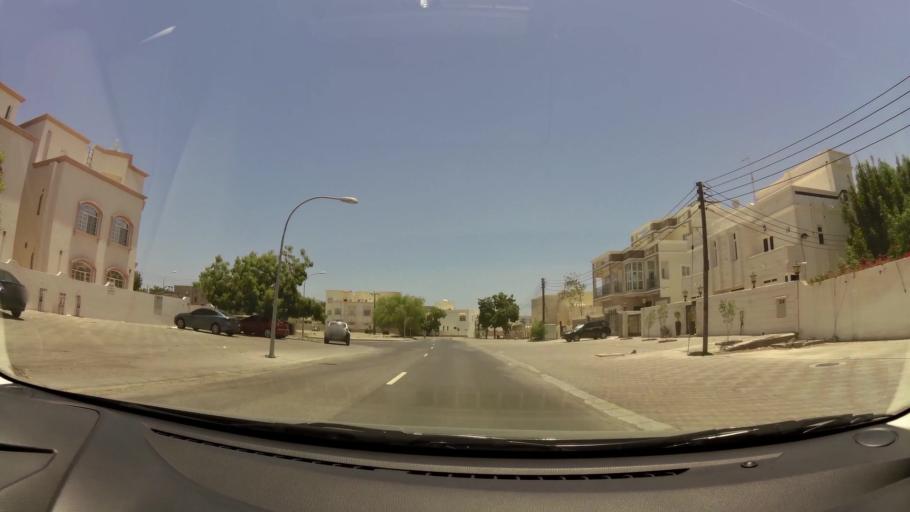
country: OM
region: Muhafazat Masqat
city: As Sib al Jadidah
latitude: 23.6342
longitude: 58.2388
